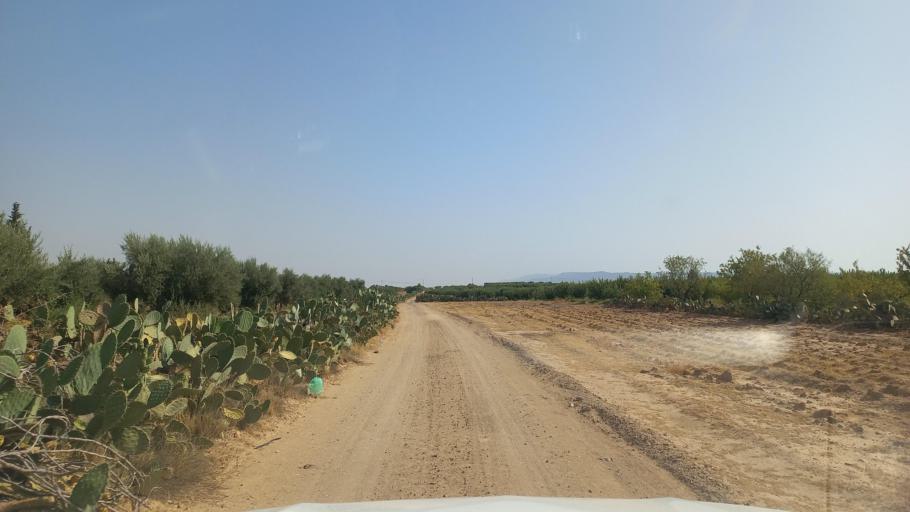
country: TN
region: Al Qasrayn
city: Kasserine
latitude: 35.2427
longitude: 9.0280
